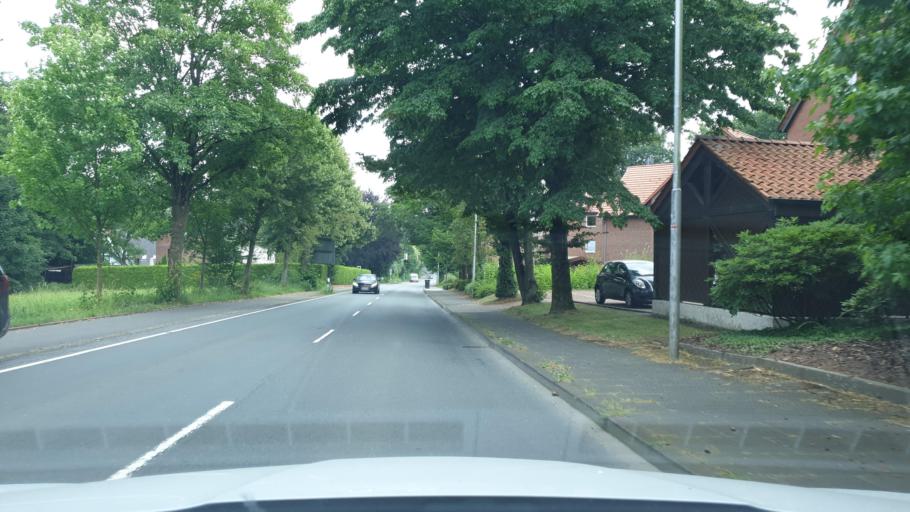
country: DE
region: North Rhine-Westphalia
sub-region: Regierungsbezirk Detmold
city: Bad Salzuflen
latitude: 52.1365
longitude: 8.7794
